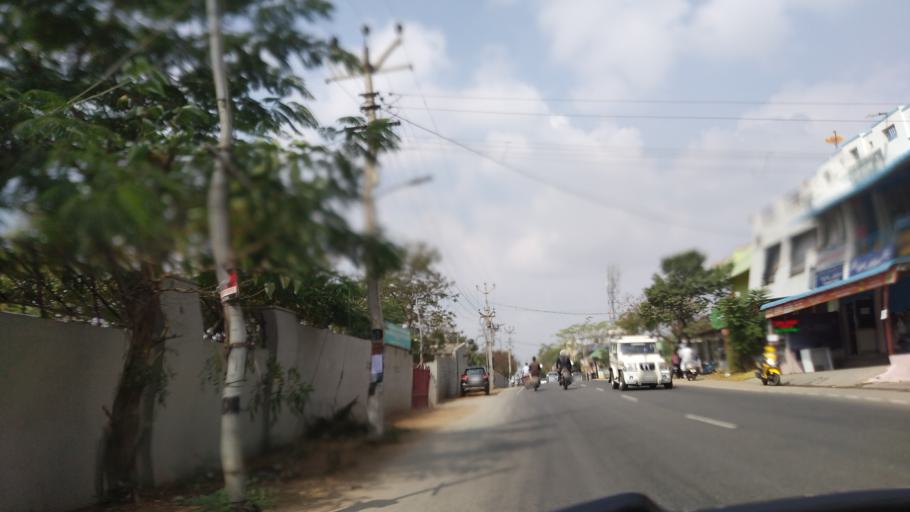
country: IN
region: Tamil Nadu
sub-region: Coimbatore
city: Madukkarai
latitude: 10.9395
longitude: 76.9456
